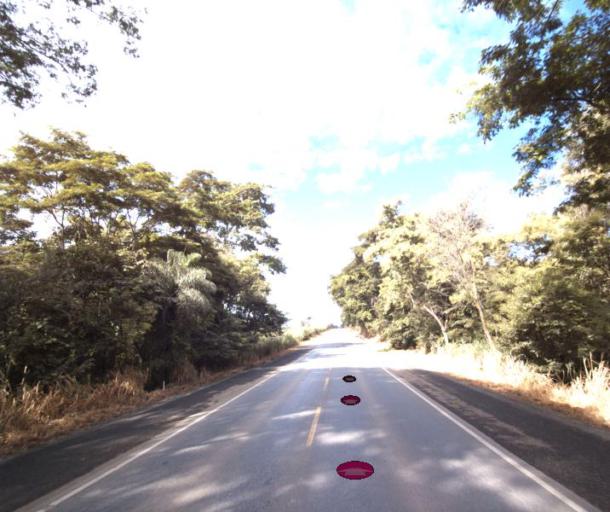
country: BR
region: Goias
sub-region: Uruacu
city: Uruacu
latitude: -14.7354
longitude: -49.2419
